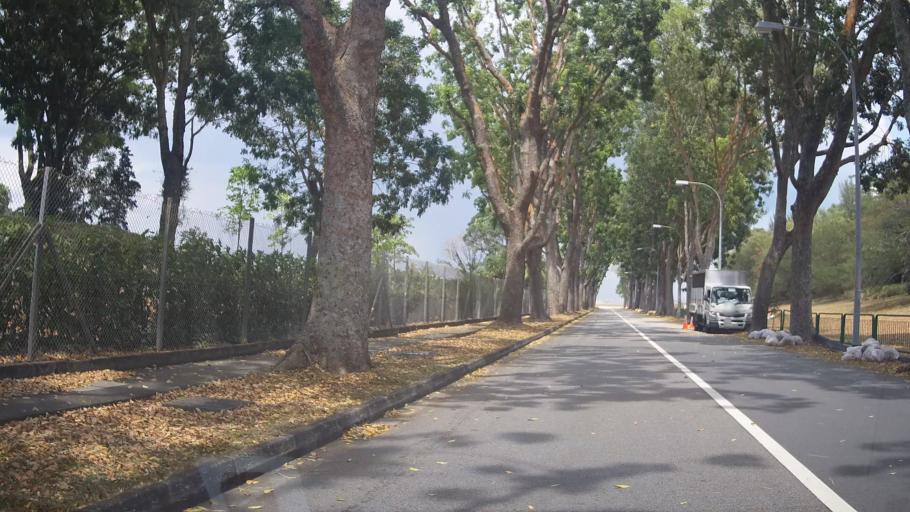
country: SG
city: Singapore
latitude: 1.3183
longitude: 103.9784
